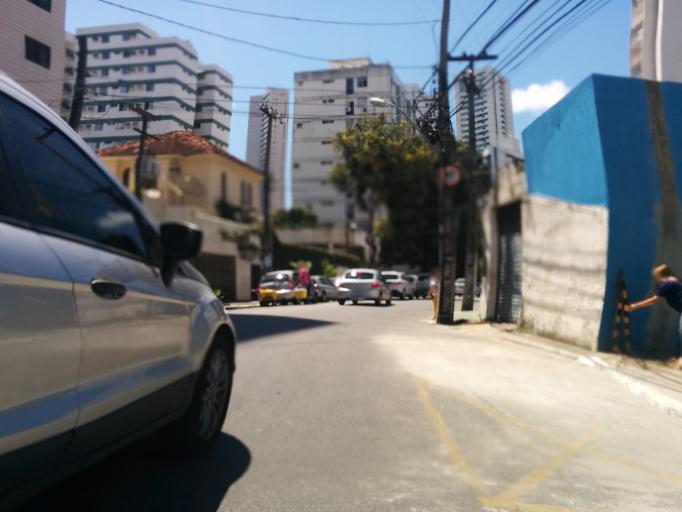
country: BR
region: Pernambuco
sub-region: Recife
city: Recife
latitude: -8.0425
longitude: -34.8987
